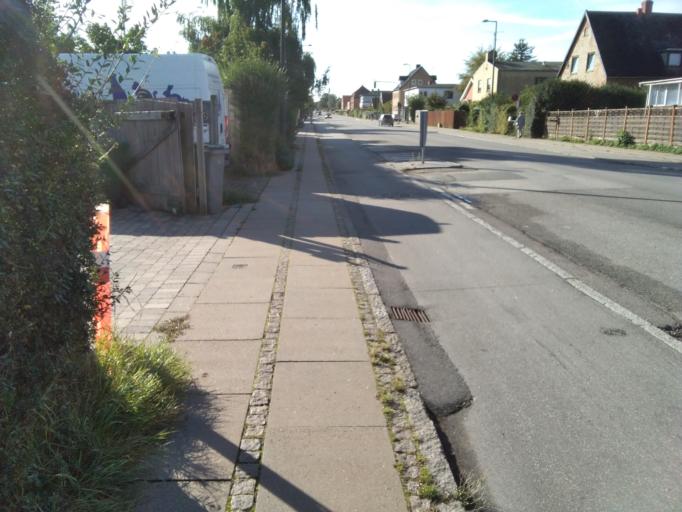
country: DK
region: Capital Region
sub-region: Kobenhavn
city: Vanlose
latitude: 55.7064
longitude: 12.4783
